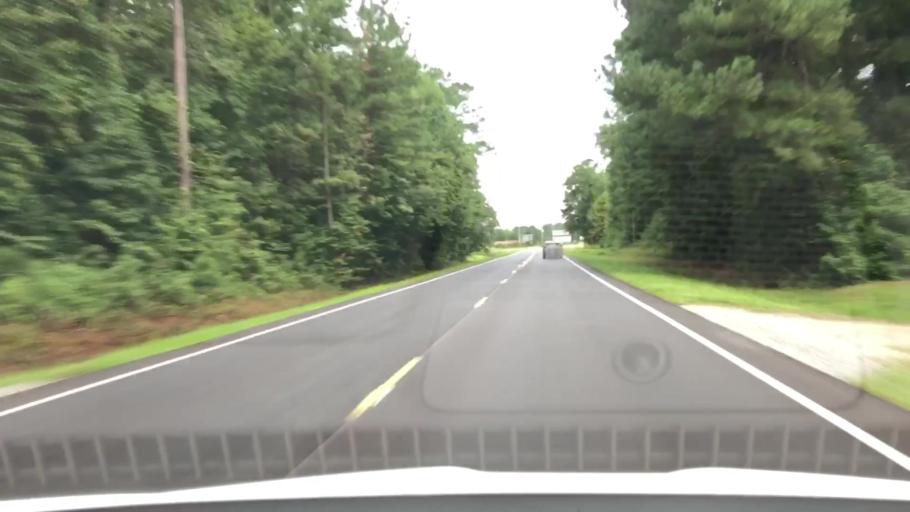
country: US
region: North Carolina
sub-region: Jones County
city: Maysville
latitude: 34.8594
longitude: -77.1872
